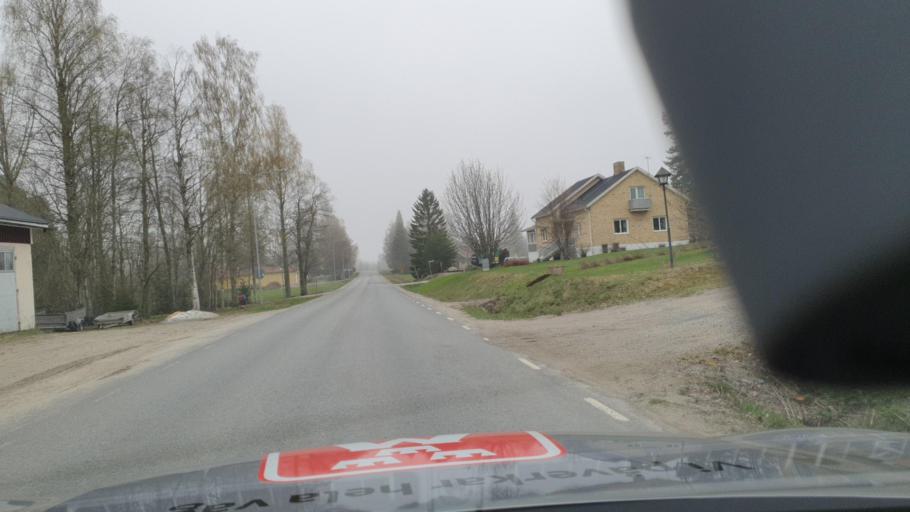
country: SE
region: Vaesternorrland
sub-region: OErnskoeldsviks Kommun
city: Husum
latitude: 63.4835
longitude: 18.9757
